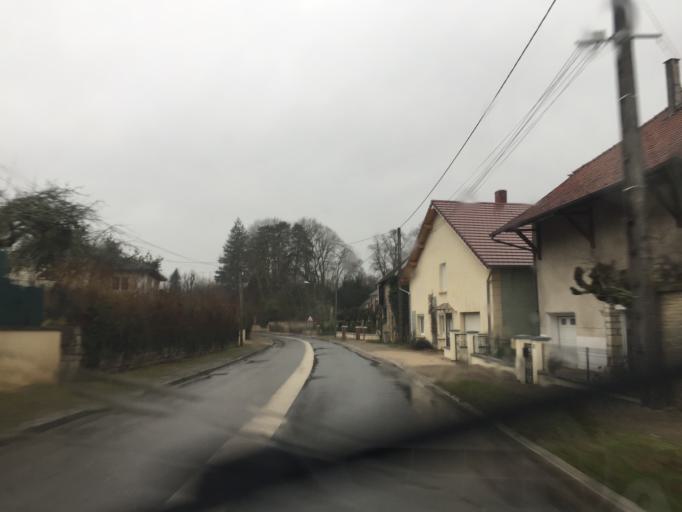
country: FR
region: Franche-Comte
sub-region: Departement du Doubs
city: Arc-et-Senans
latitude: 46.9990
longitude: 5.7543
